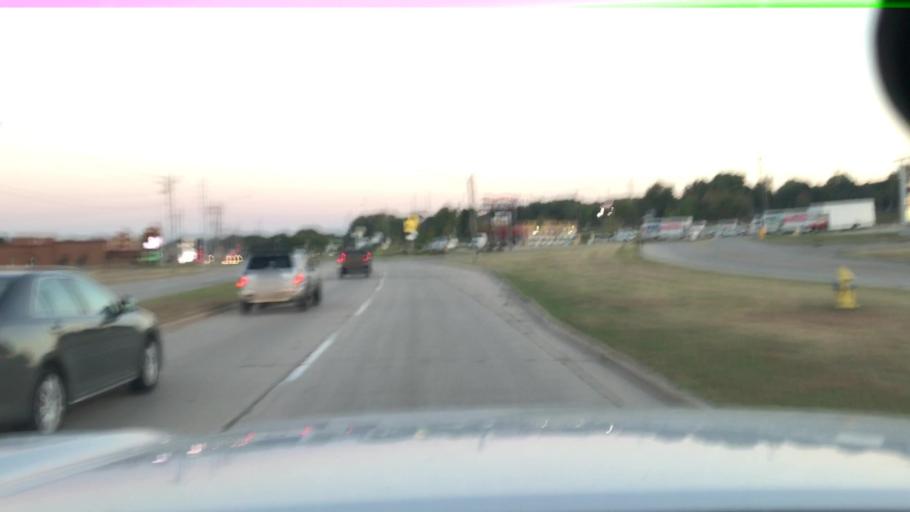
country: US
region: Wisconsin
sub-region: Brown County
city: Allouez
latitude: 44.4855
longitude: -87.9710
